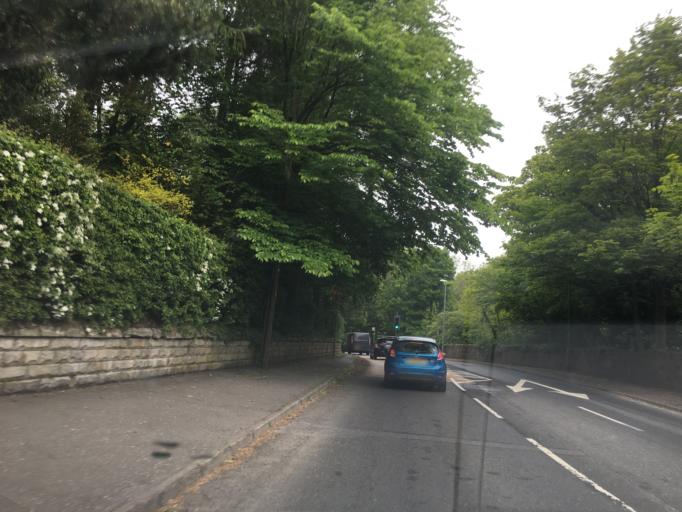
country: GB
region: Scotland
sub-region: Midlothian
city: Penicuik
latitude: 55.8440
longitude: -3.1936
